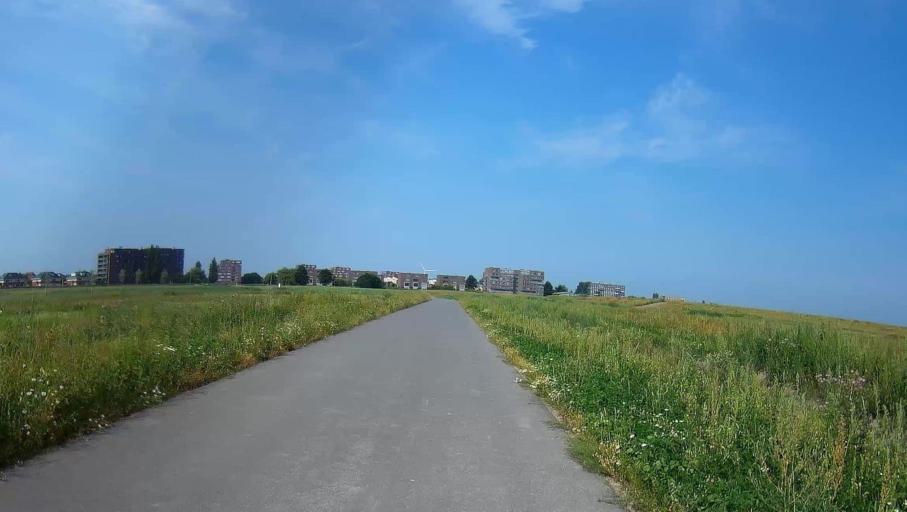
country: NL
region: South Holland
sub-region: Gemeente Pijnacker-Nootdorp
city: Pijnacker
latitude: 52.0610
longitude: 4.4256
